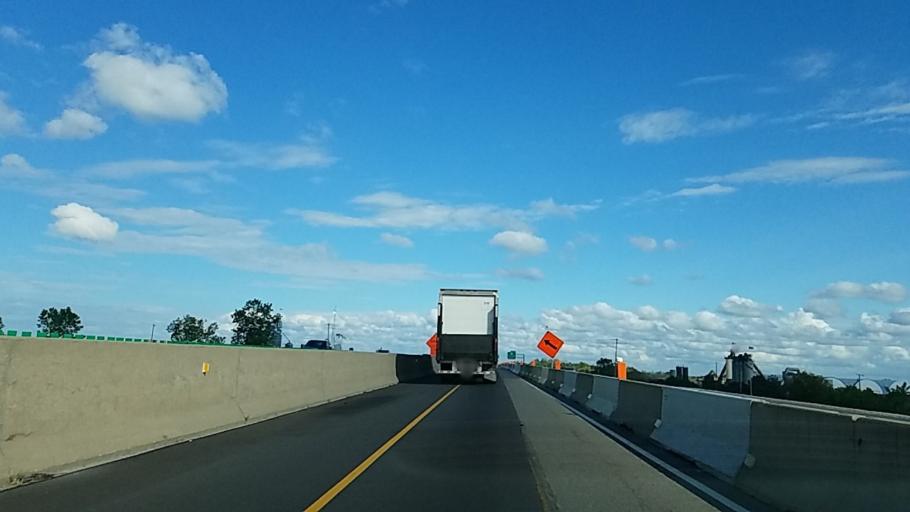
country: US
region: Ohio
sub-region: Huron County
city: Bellevue
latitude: 41.3452
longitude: -82.7884
